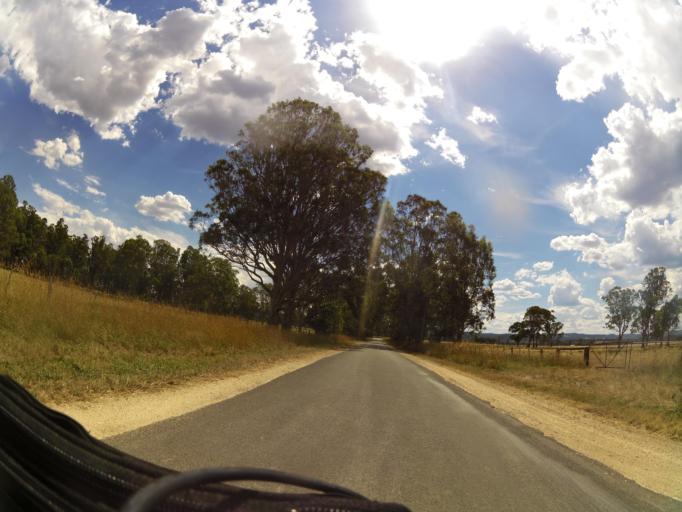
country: AU
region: Victoria
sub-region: Wellington
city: Heyfield
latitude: -37.9828
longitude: 146.7123
